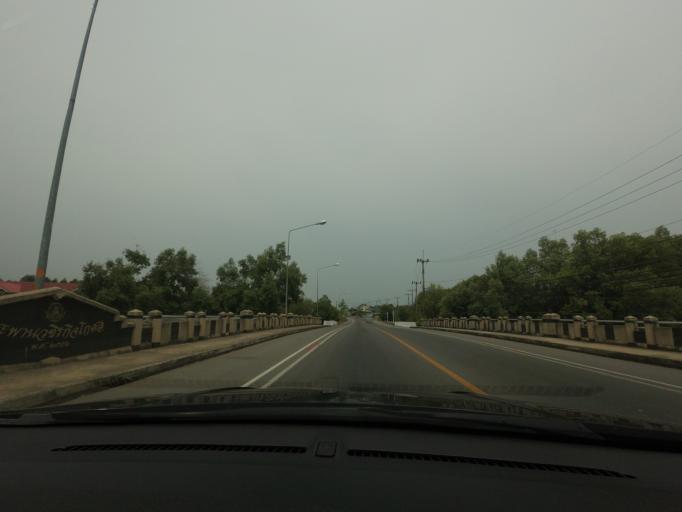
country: TH
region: Phetchaburi
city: Ban Laem
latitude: 13.2729
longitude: 99.9329
